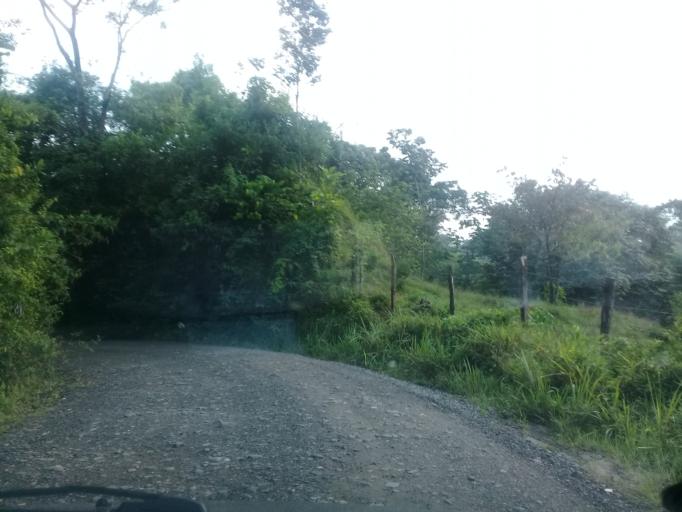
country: CO
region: Antioquia
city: Puerto Triunfo
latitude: 5.7341
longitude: -74.4744
